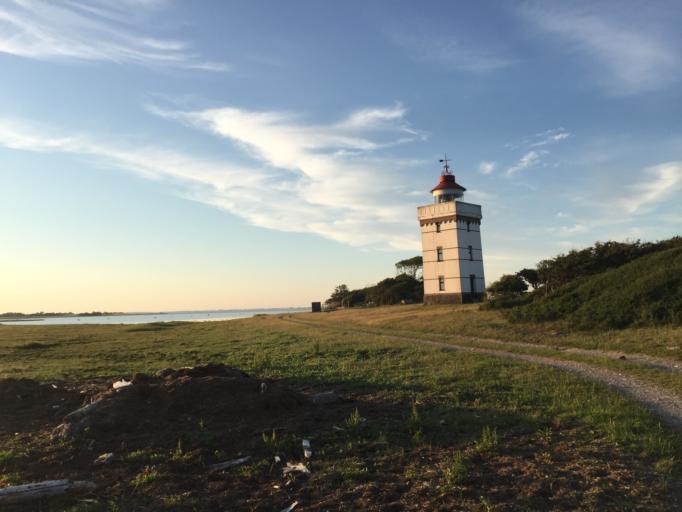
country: DK
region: Zealand
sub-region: Slagelse Kommune
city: Skaelskor
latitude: 55.1854
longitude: 11.2085
